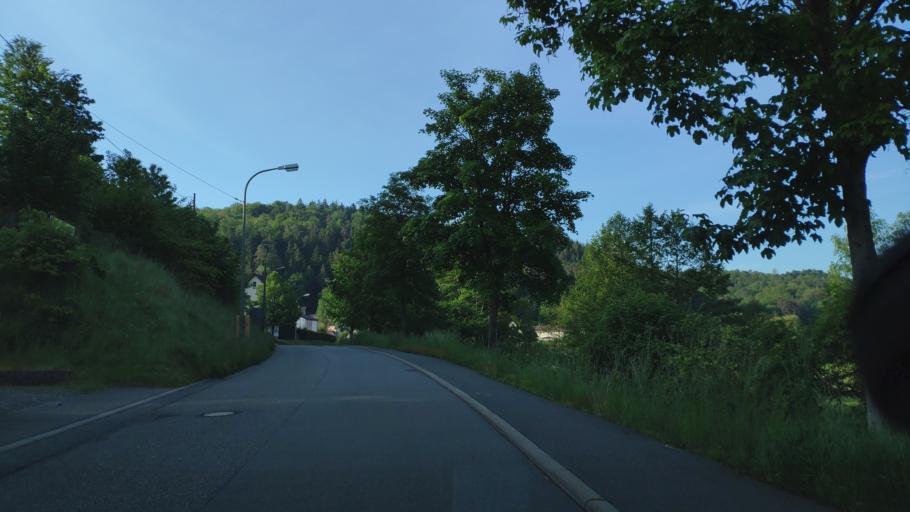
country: DE
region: Rheinland-Pfalz
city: Ruppertsweiler
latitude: 49.1689
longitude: 7.7199
